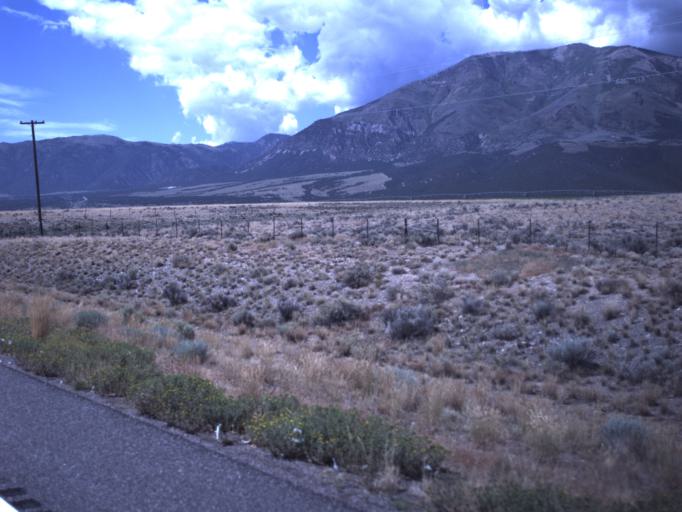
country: US
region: Utah
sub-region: Piute County
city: Junction
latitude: 38.4254
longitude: -112.2317
